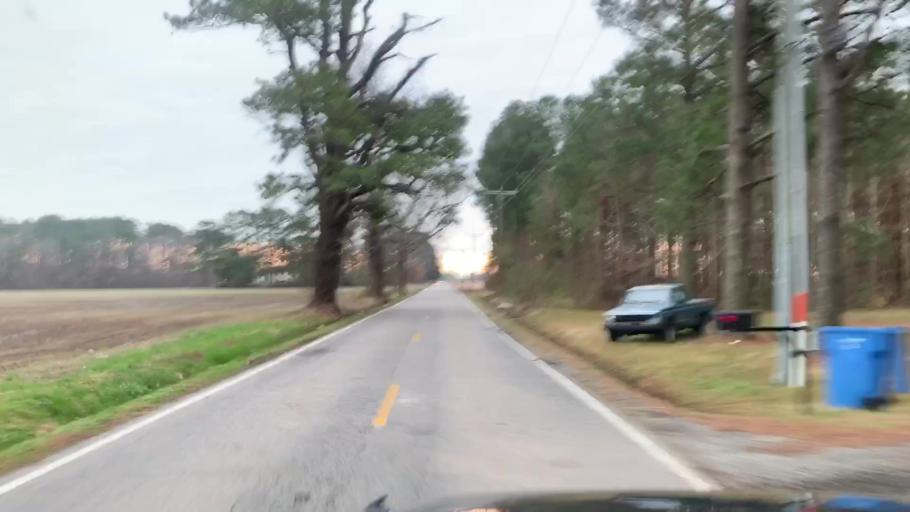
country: US
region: North Carolina
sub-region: Currituck County
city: Moyock
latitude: 36.6318
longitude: -76.1797
